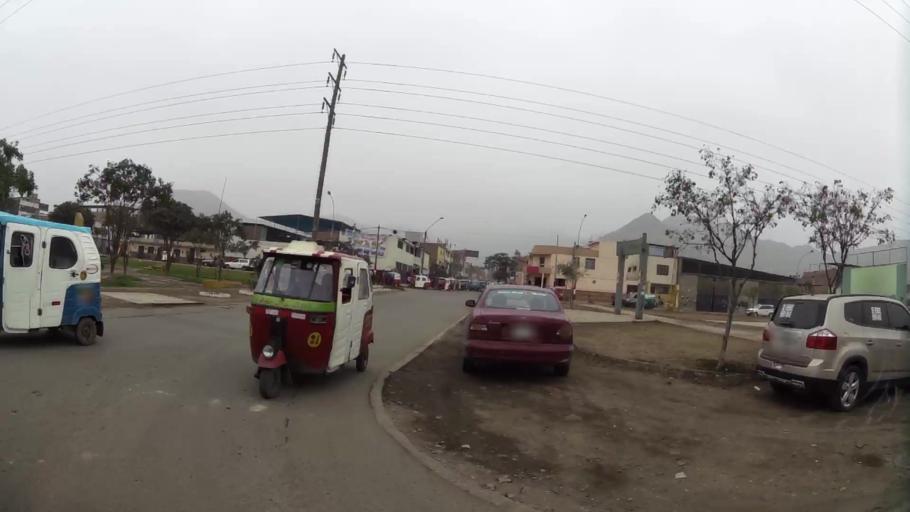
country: PE
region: Lima
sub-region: Lima
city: Surco
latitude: -12.1679
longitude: -76.9491
